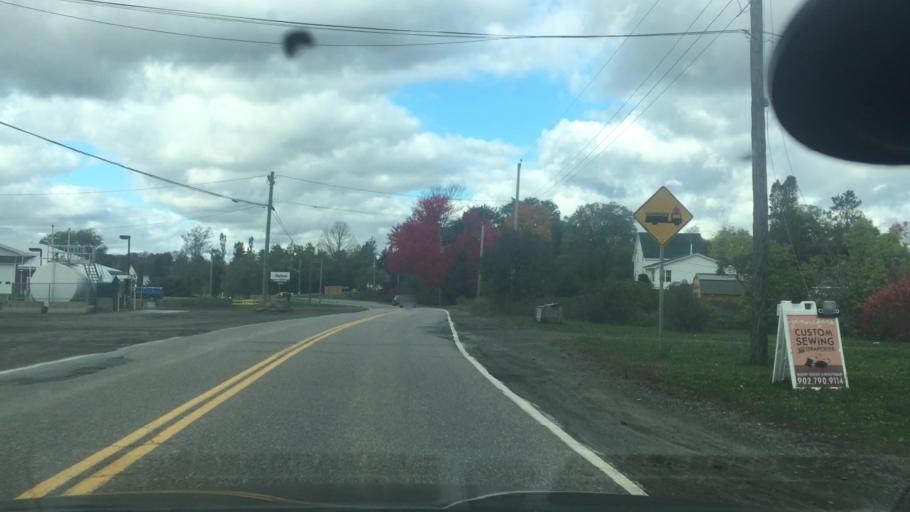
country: CA
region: Nova Scotia
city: Windsor
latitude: 44.9739
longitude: -64.1030
